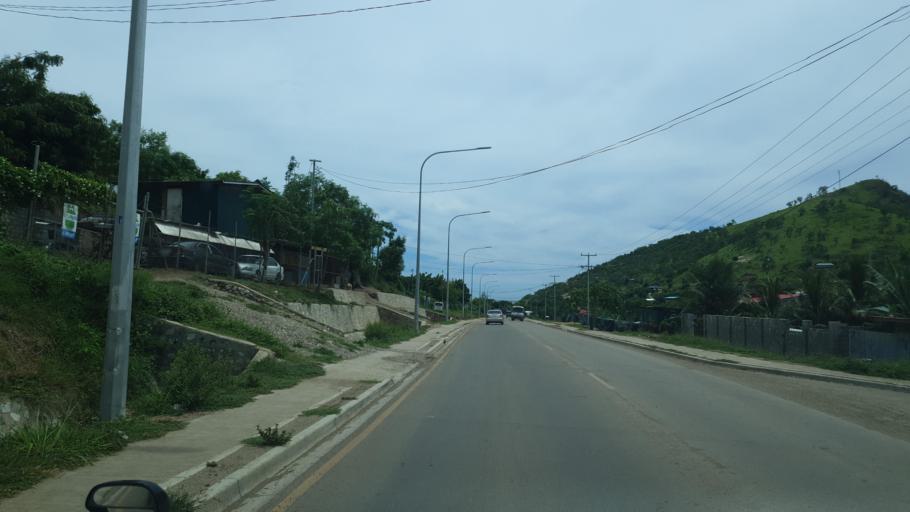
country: PG
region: National Capital
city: Port Moresby
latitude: -9.5255
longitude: 147.2412
